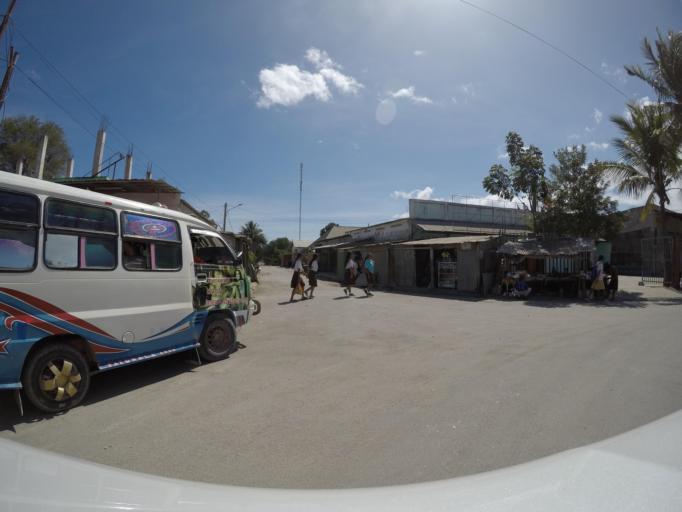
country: TL
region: Baucau
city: Baucau
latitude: -8.4789
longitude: 126.4527
